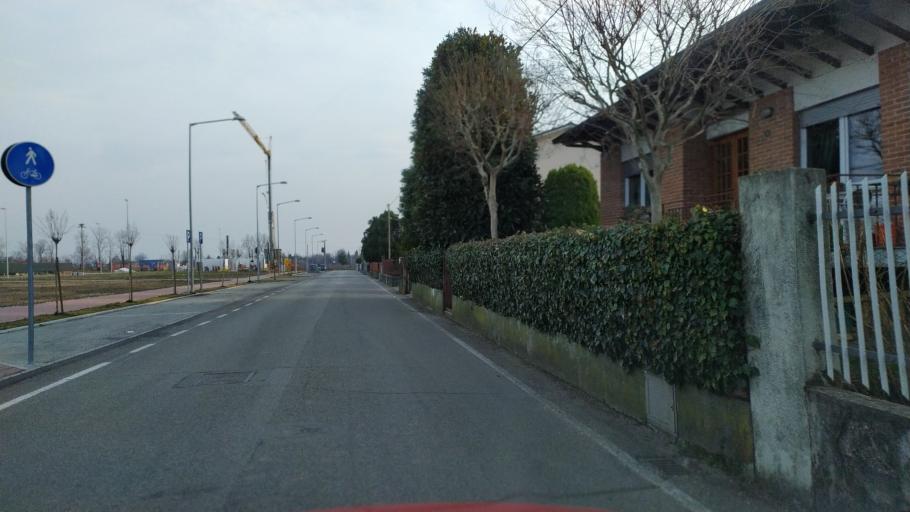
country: IT
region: Veneto
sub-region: Provincia di Vicenza
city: Marano Vicentino
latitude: 45.6869
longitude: 11.4314
